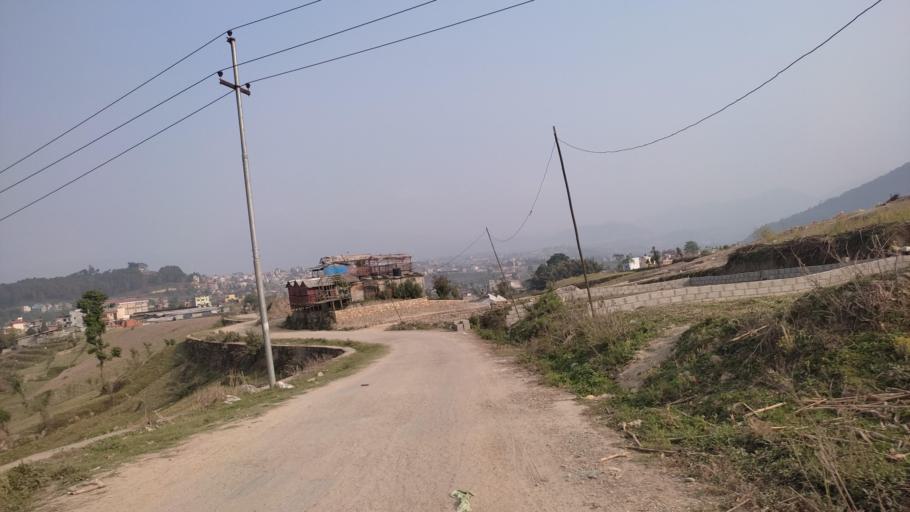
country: NP
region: Central Region
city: Kirtipur
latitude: 27.6610
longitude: 85.2831
